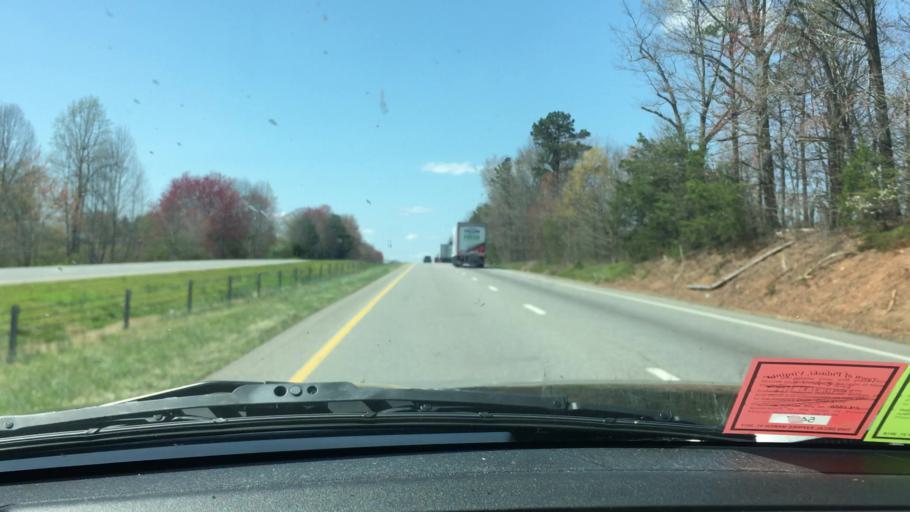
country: US
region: North Carolina
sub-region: Surry County
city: Pilot Mountain
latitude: 36.4163
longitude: -80.5089
